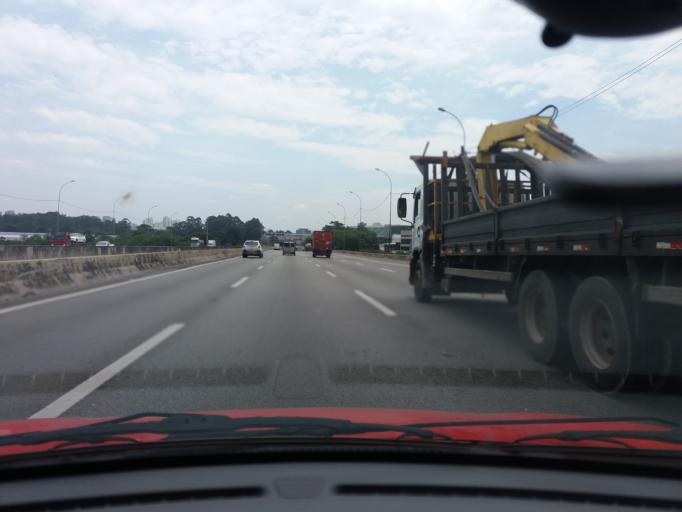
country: BR
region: Sao Paulo
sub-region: Carapicuiba
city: Carapicuiba
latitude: -23.5144
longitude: -46.8168
